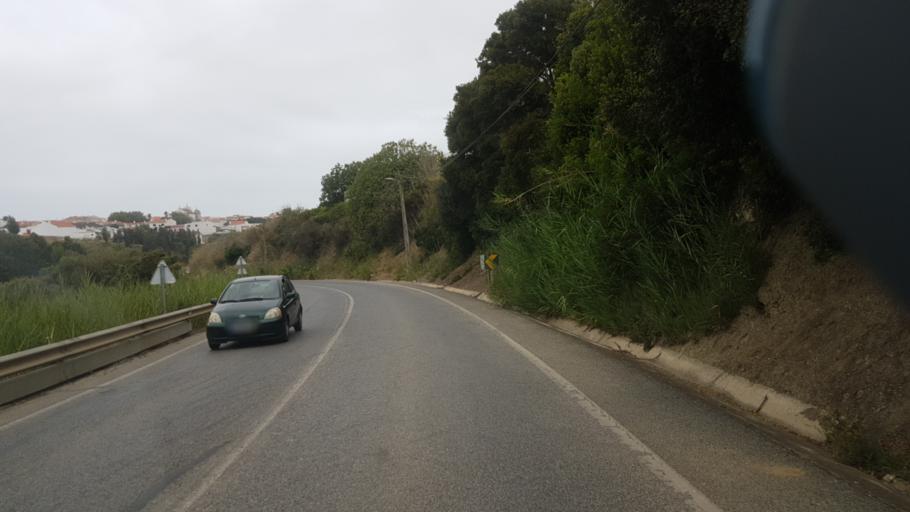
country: PT
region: Leiria
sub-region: Peniche
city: Atouguia da Baleia
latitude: 39.3378
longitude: -9.3186
